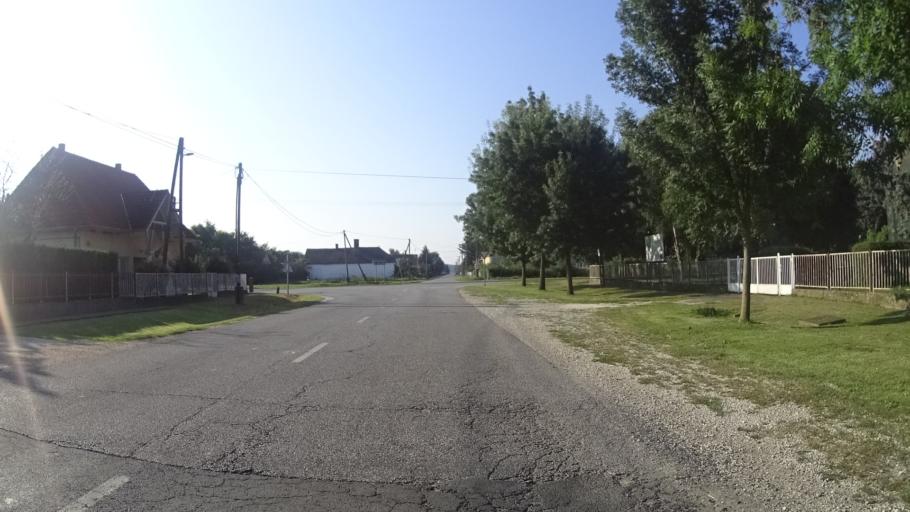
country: HU
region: Zala
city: Sarmellek
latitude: 46.6679
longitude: 17.1582
